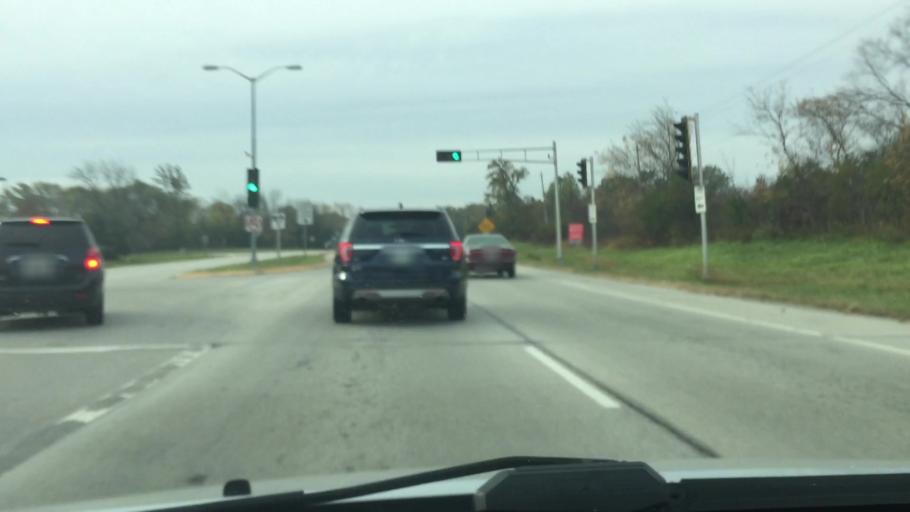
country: US
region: Wisconsin
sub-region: Milwaukee County
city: Franklin
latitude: 42.9038
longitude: -88.0393
